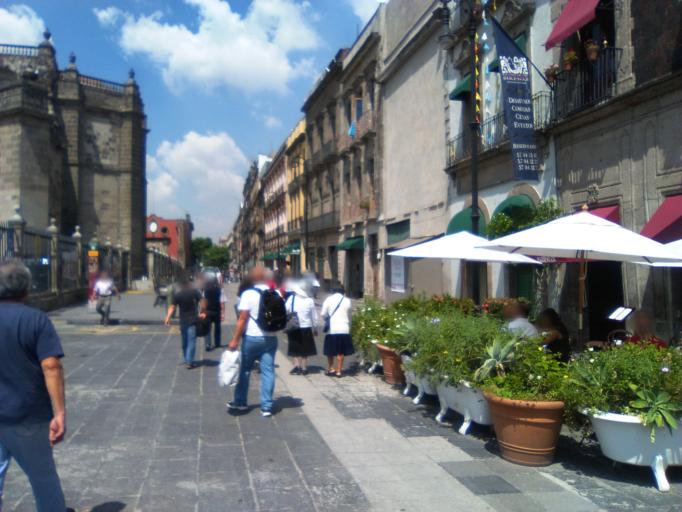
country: MX
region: Mexico City
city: Mexico City
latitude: 19.4349
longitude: -99.1323
